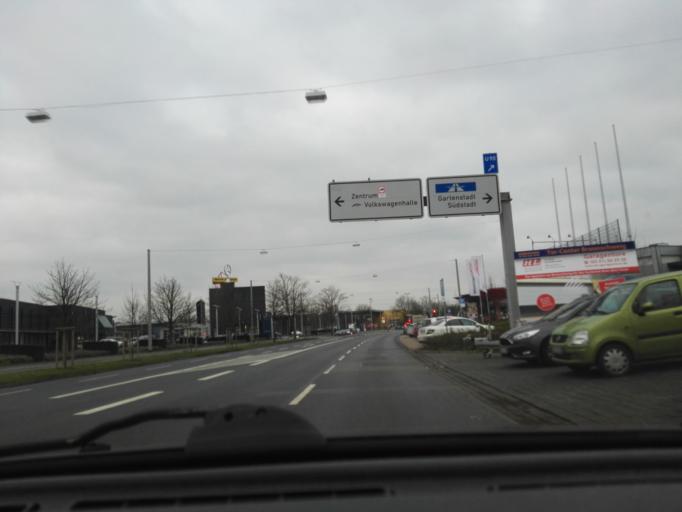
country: DE
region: Lower Saxony
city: Braunschweig
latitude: 52.2479
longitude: 10.5113
